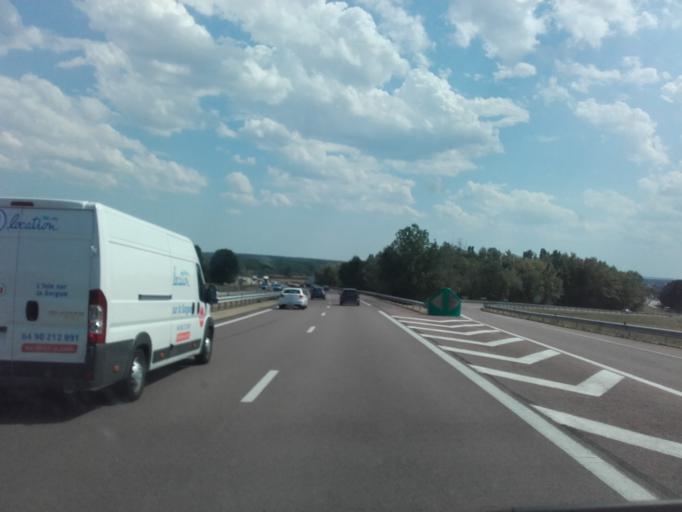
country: FR
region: Bourgogne
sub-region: Departement de l'Yonne
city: Avallon
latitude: 47.5167
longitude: 3.9909
